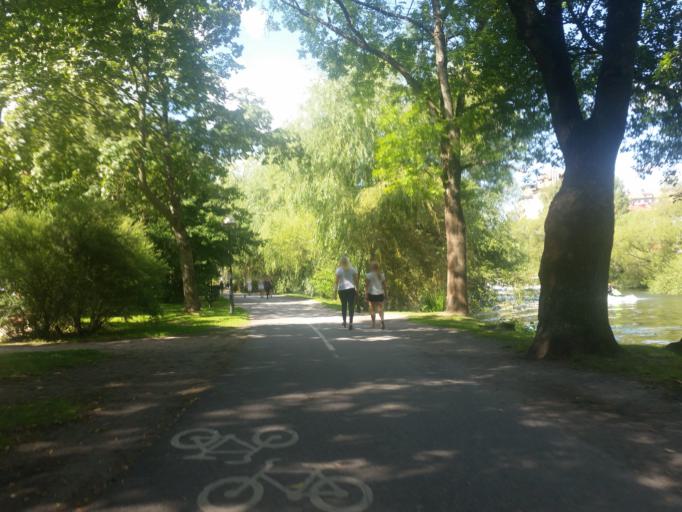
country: SE
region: Stockholm
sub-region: Stockholms Kommun
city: Stockholm
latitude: 59.3360
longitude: 18.0410
